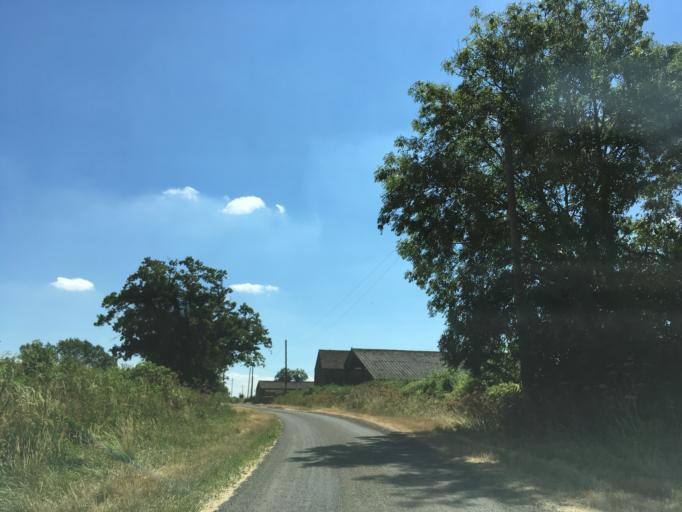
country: GB
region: England
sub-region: Wiltshire
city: Luckington
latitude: 51.5656
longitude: -2.2130
